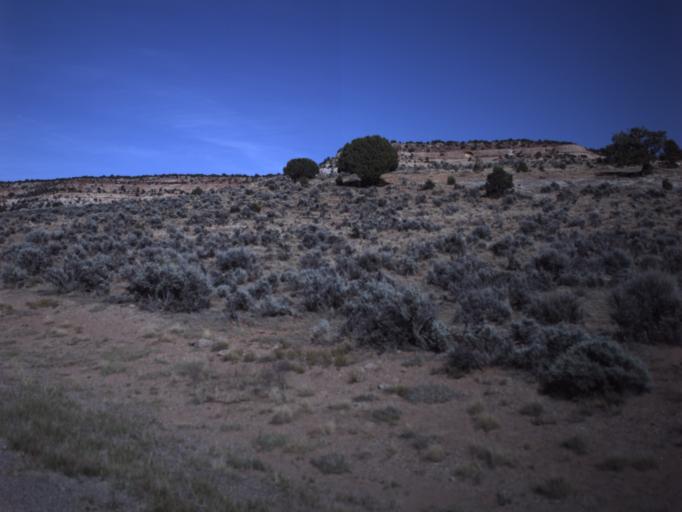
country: US
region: Utah
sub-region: San Juan County
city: Monticello
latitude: 38.0315
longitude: -109.4206
